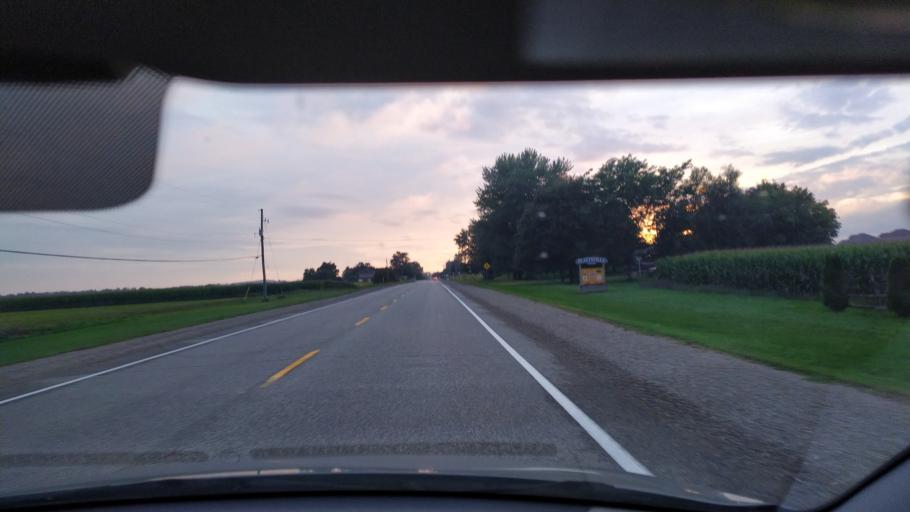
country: CA
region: Ontario
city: Kitchener
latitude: 43.3057
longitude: -80.6066
